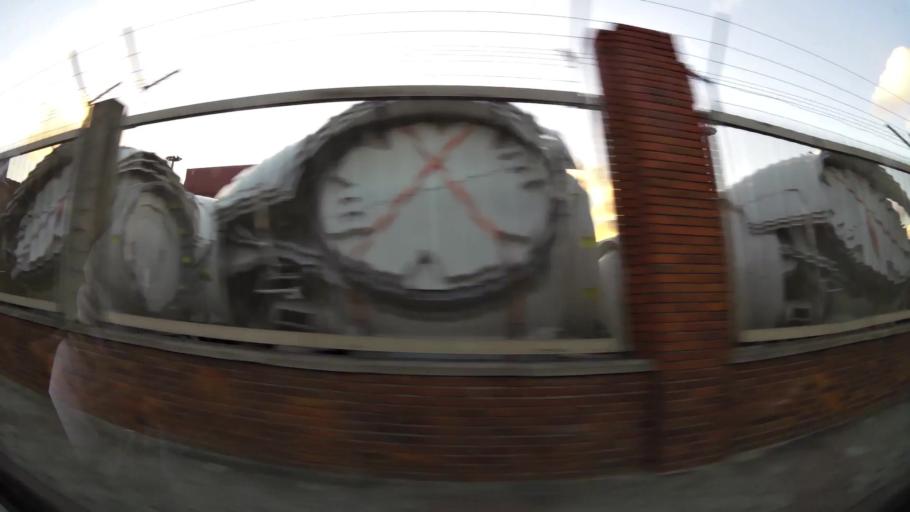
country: UY
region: Montevideo
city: Montevideo
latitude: -34.8980
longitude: -56.1949
